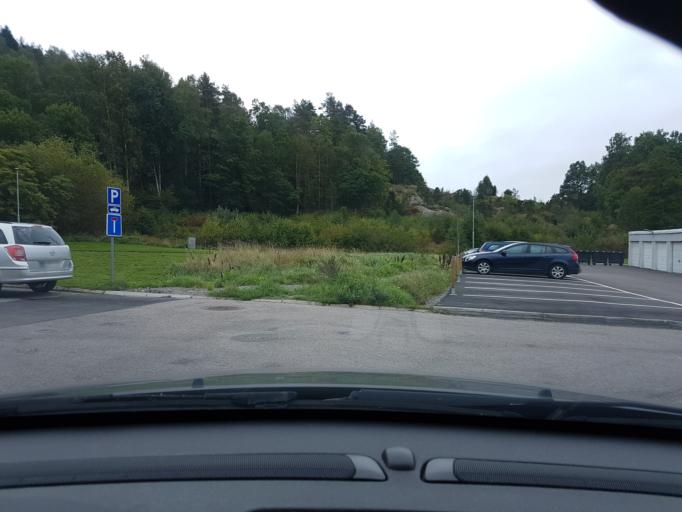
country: SE
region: Vaestra Goetaland
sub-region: Ale Kommun
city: Nodinge-Nol
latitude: 57.9105
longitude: 12.0698
